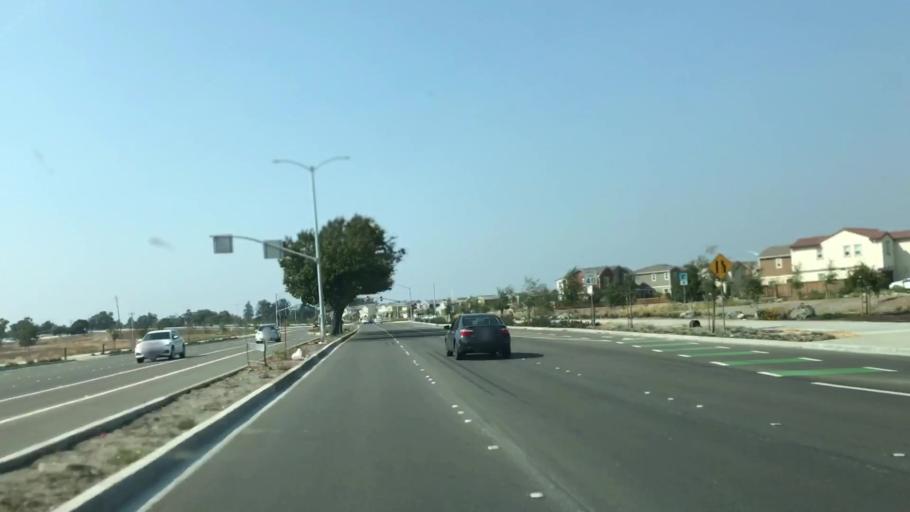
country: US
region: California
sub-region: Alameda County
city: Newark
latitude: 37.5607
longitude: -122.0640
